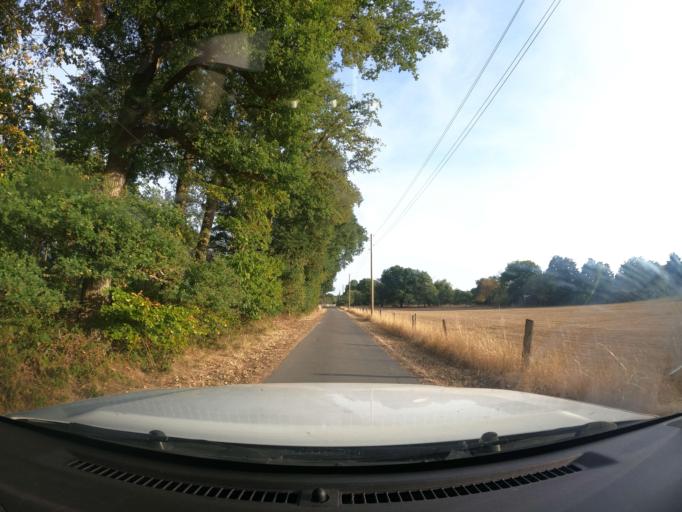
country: DE
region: North Rhine-Westphalia
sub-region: Regierungsbezirk Dusseldorf
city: Hamminkeln
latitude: 51.7073
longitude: 6.5680
